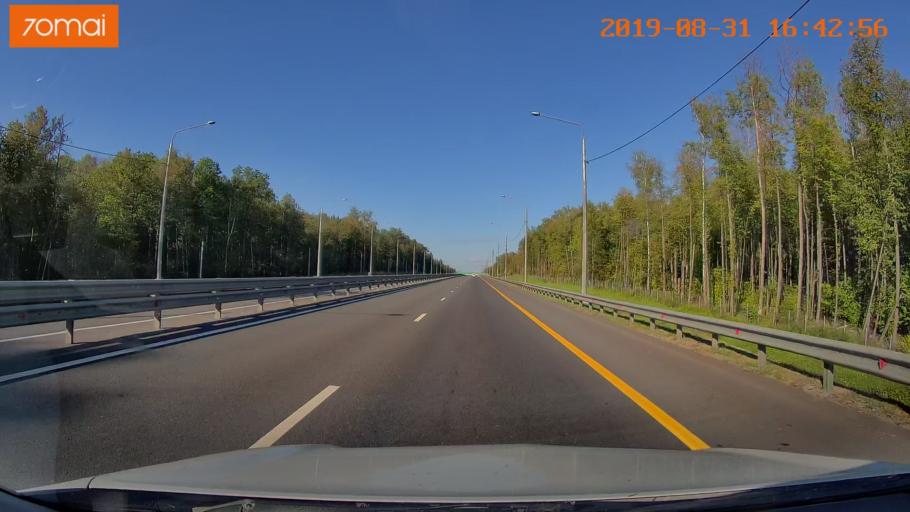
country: RU
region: Kaluga
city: Mstikhino
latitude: 54.6018
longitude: 36.0950
